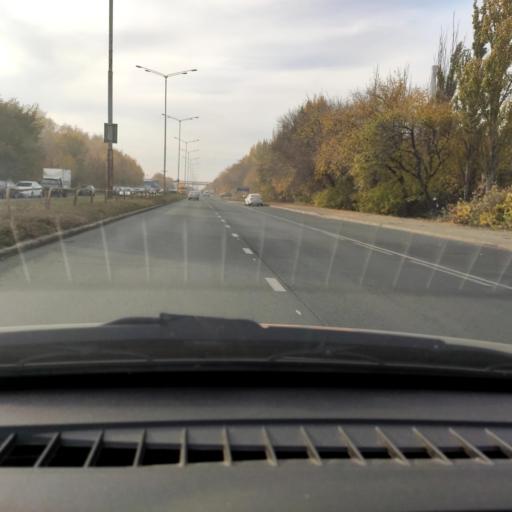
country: RU
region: Samara
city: Tol'yatti
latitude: 53.5698
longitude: 49.2563
